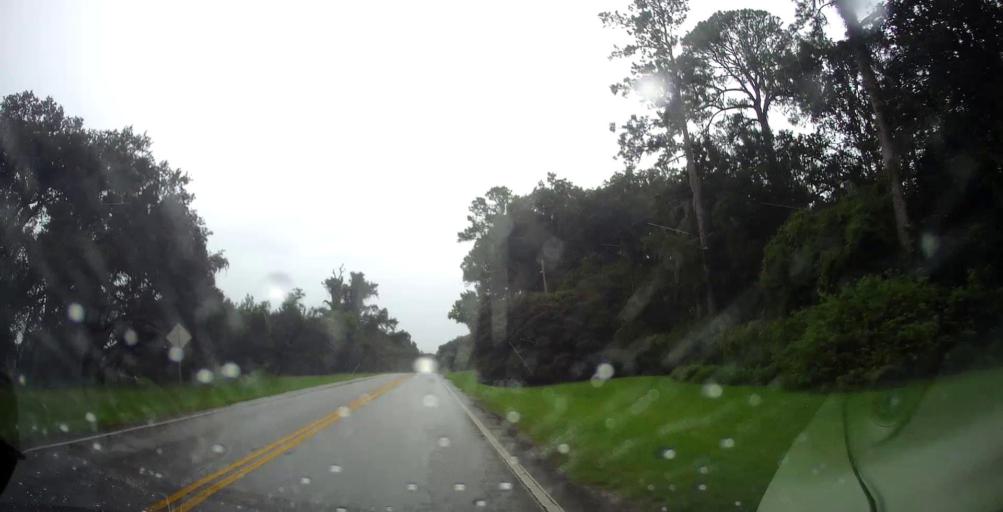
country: US
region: Florida
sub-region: Marion County
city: Citra
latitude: 29.4049
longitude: -82.2504
